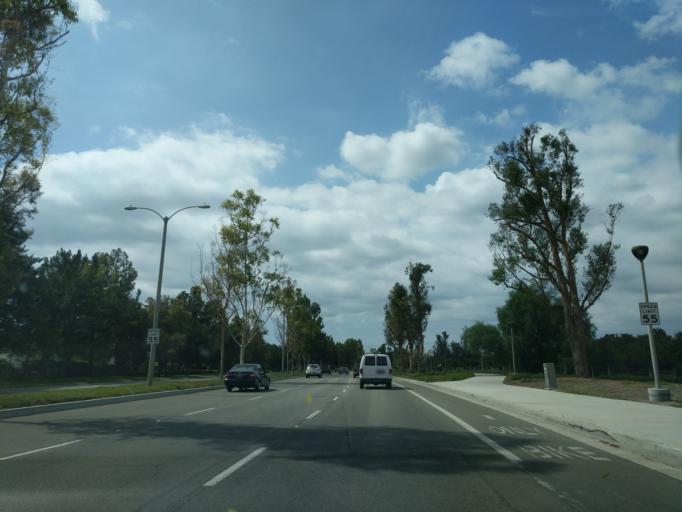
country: US
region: California
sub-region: Orange County
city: North Tustin
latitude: 33.7303
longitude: -117.7540
